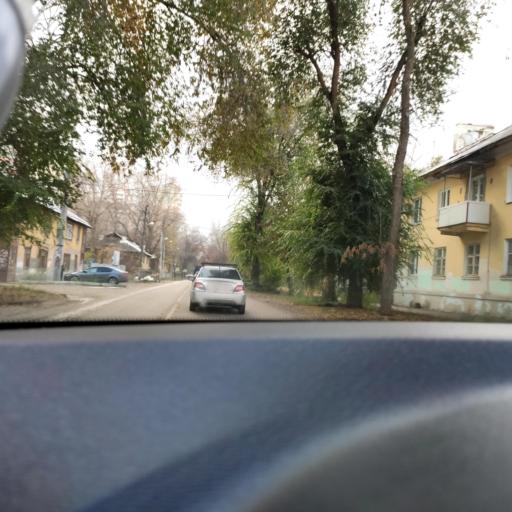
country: RU
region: Samara
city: Samara
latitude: 53.2310
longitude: 50.2647
